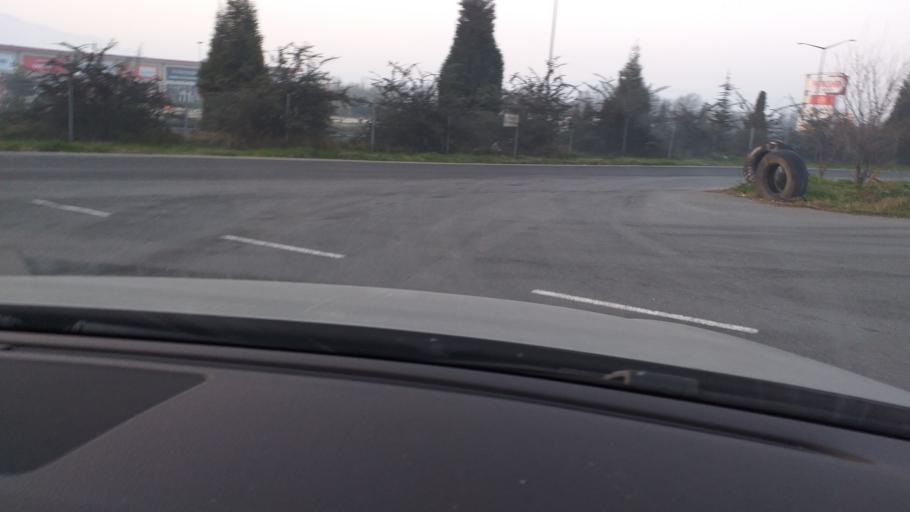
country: TR
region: Sakarya
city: Hendek
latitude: 40.7525
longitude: 30.6950
